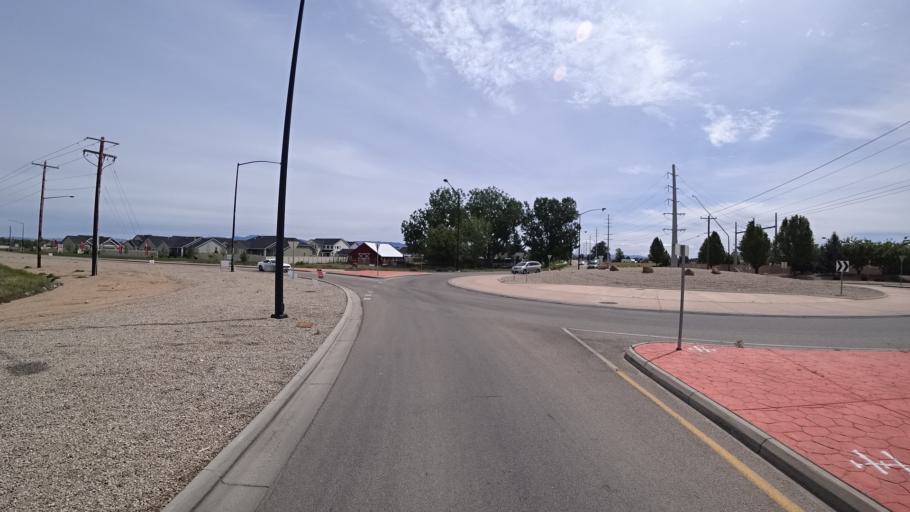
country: US
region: Idaho
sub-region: Ada County
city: Meridian
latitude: 43.5613
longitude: -116.3547
